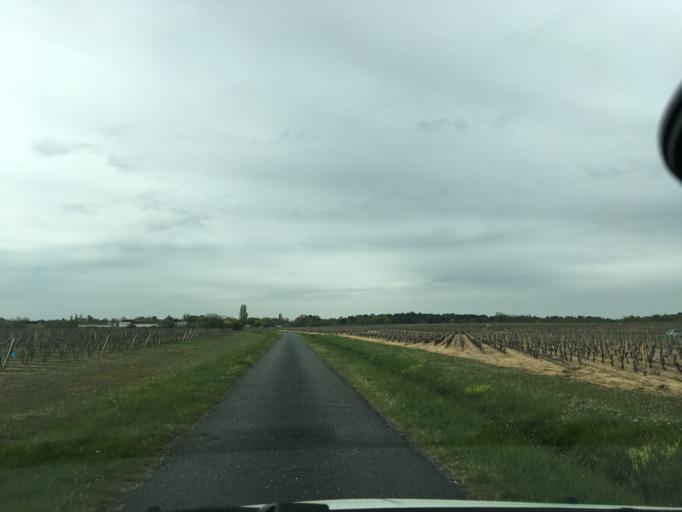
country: FR
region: Aquitaine
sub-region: Departement de la Gironde
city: Lesparre-Medoc
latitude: 45.3215
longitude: -0.8952
